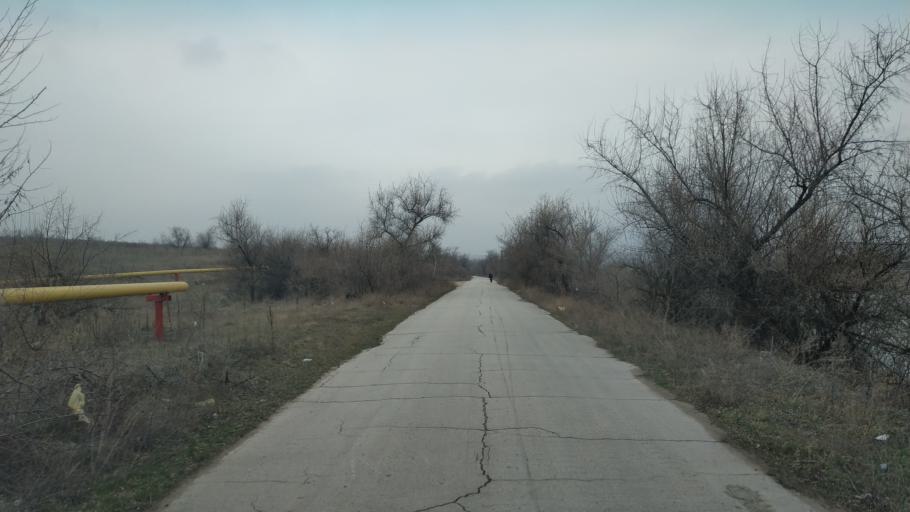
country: MD
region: Chisinau
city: Singera
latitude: 46.9176
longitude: 29.0089
